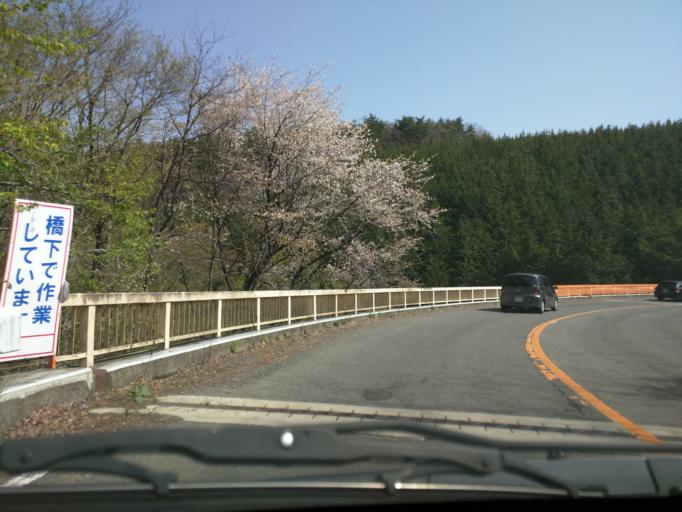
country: JP
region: Fukushima
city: Nihommatsu
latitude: 37.6030
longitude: 140.3707
